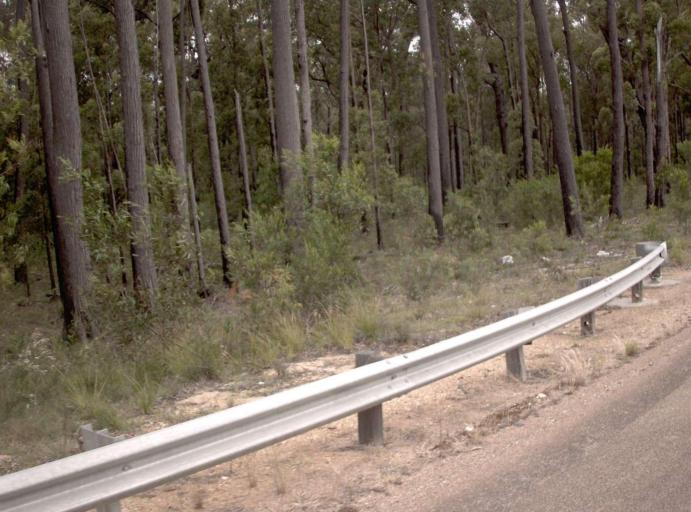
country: AU
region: Victoria
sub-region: East Gippsland
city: Lakes Entrance
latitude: -37.6957
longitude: 148.0469
